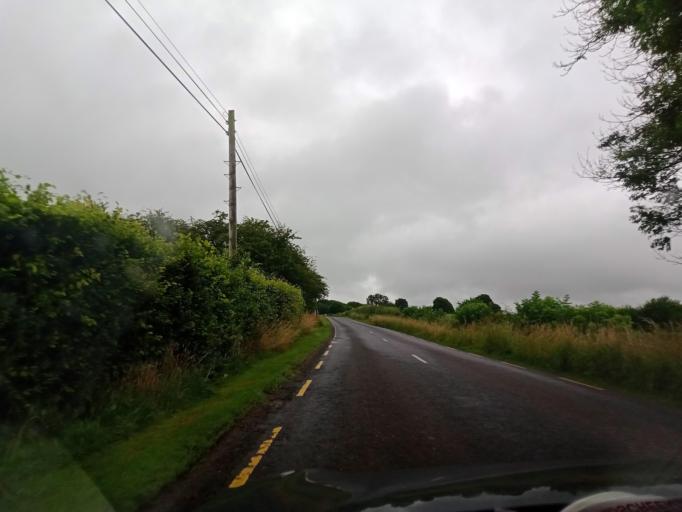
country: IE
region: Leinster
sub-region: Laois
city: Abbeyleix
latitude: 52.9100
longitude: -7.3017
